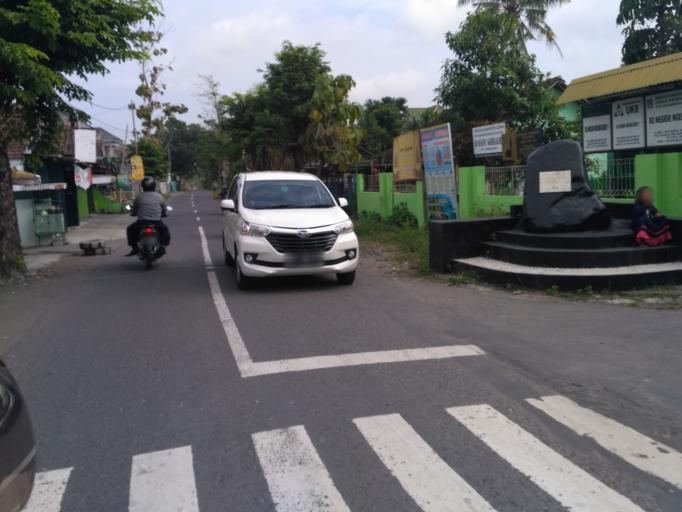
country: ID
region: Daerah Istimewa Yogyakarta
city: Melati
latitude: -7.7199
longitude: 110.4000
